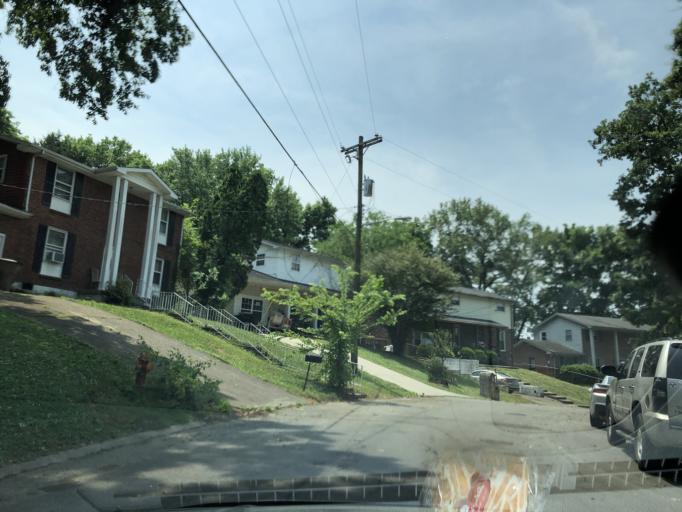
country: US
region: Tennessee
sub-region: Rutherford County
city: La Vergne
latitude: 36.0729
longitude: -86.6725
